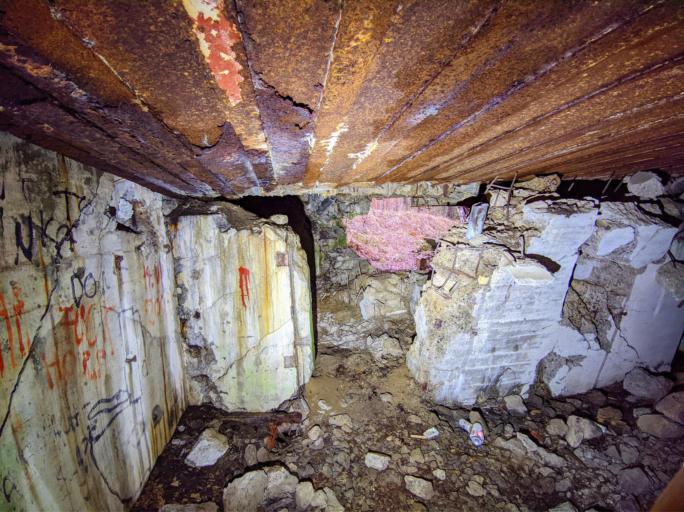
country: PL
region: Lubusz
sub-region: Powiat swiebodzinski
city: Miedzylesie
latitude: 52.0906
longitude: 15.3906
